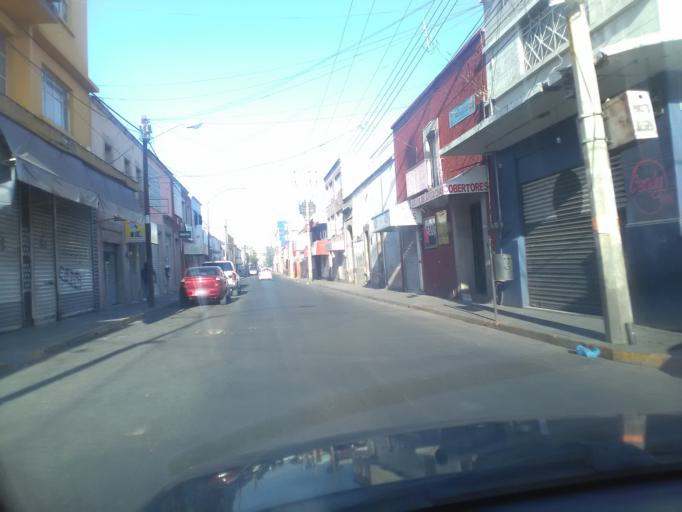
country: MX
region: Durango
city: Victoria de Durango
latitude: 24.0228
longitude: -104.6661
